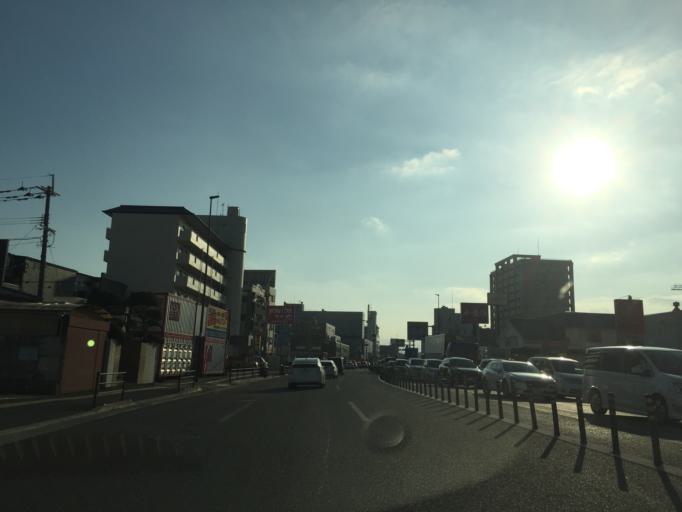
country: JP
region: Fukuoka
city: Fukuoka-shi
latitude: 33.6218
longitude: 130.4195
